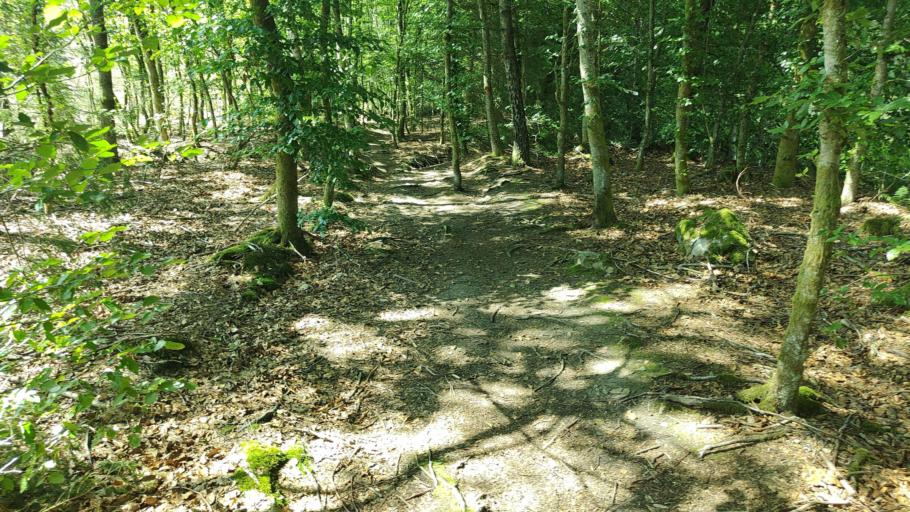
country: DE
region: North Rhine-Westphalia
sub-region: Regierungsbezirk Koln
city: Roetgen
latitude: 50.6428
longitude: 6.1678
